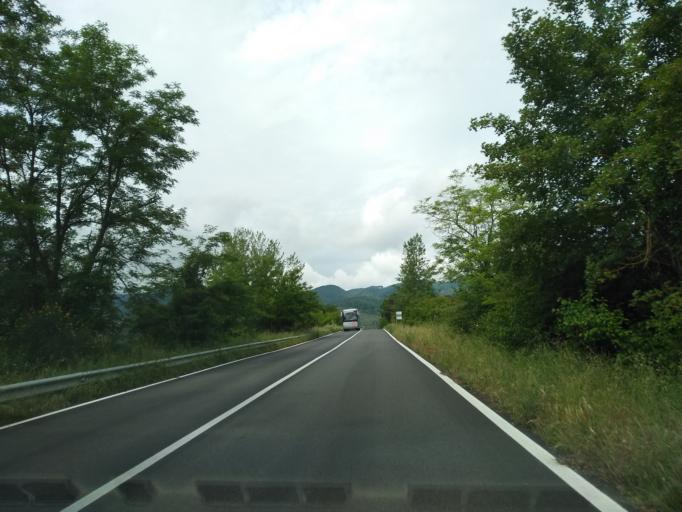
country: IT
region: Tuscany
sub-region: Province of Arezzo
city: Castelnuovo dei Sabbioni
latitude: 43.5611
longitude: 11.4602
